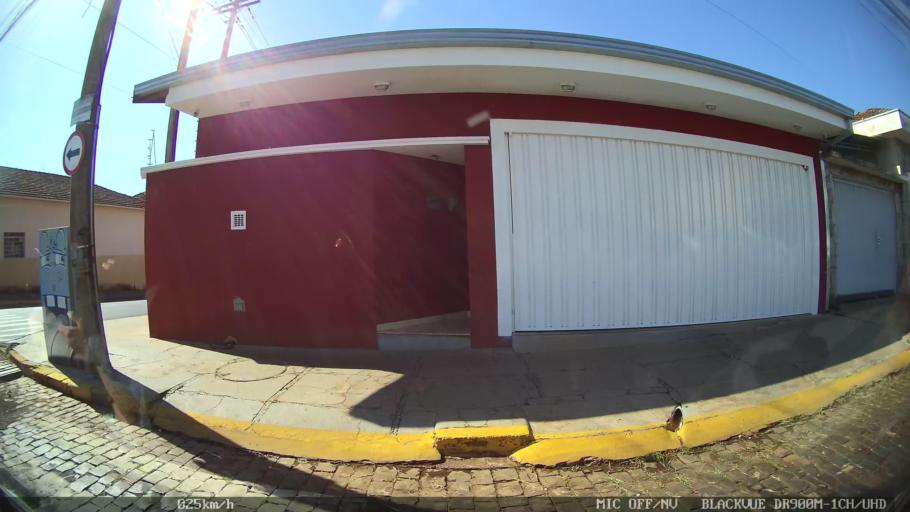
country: BR
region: Sao Paulo
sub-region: Batatais
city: Batatais
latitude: -20.8974
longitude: -47.5838
